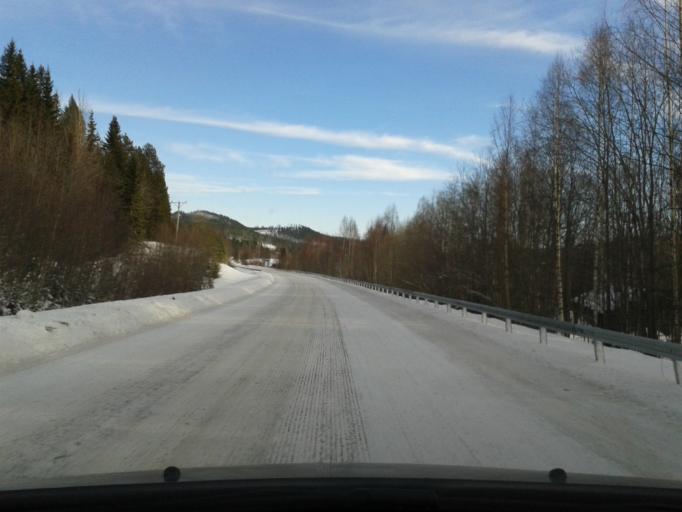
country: SE
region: Vaesterbotten
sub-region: Asele Kommun
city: Asele
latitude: 64.3230
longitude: 17.0782
